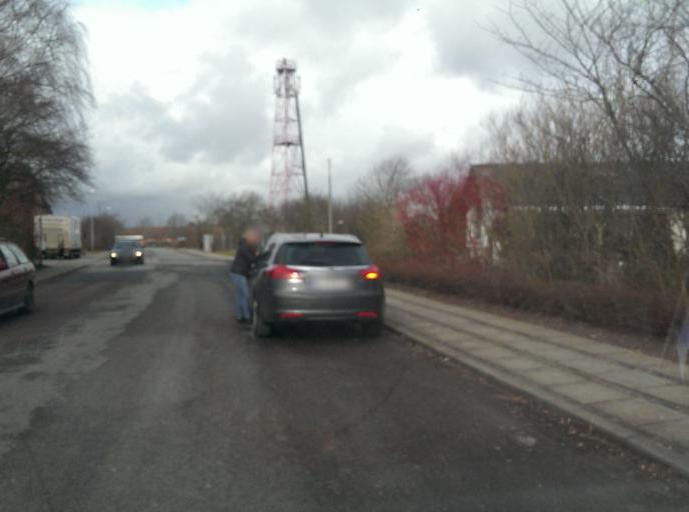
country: DK
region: South Denmark
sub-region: Esbjerg Kommune
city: Esbjerg
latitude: 55.5022
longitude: 8.4156
